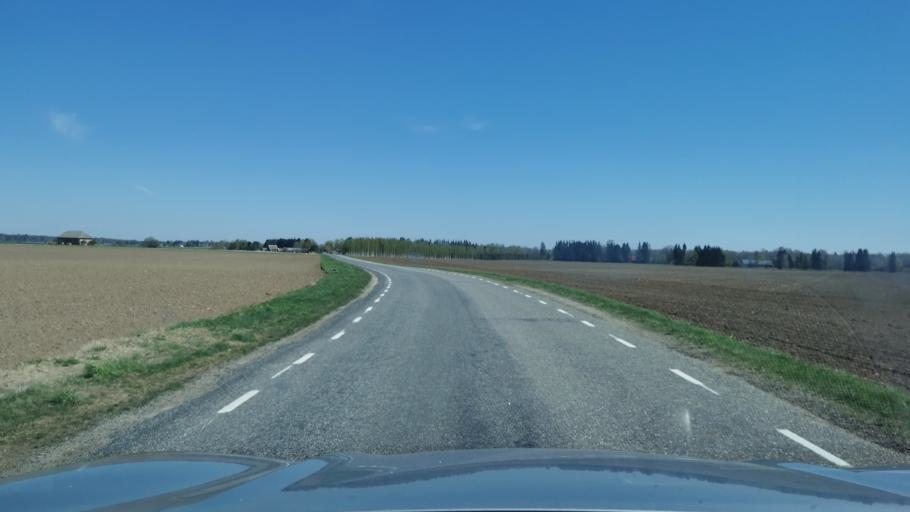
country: EE
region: Laeaene-Virumaa
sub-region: Vinni vald
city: Vinni
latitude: 59.0879
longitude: 26.6101
